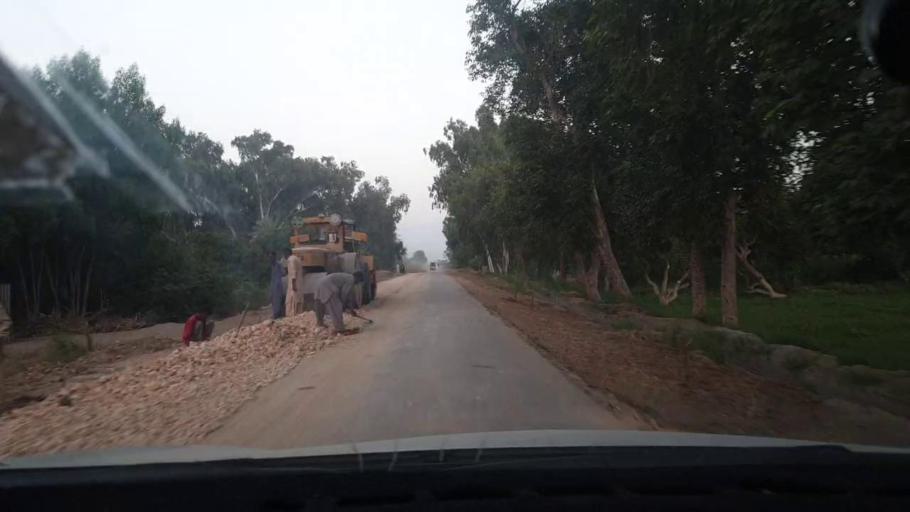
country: PK
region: Sindh
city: Bhit Shah
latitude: 25.7530
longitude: 68.5583
